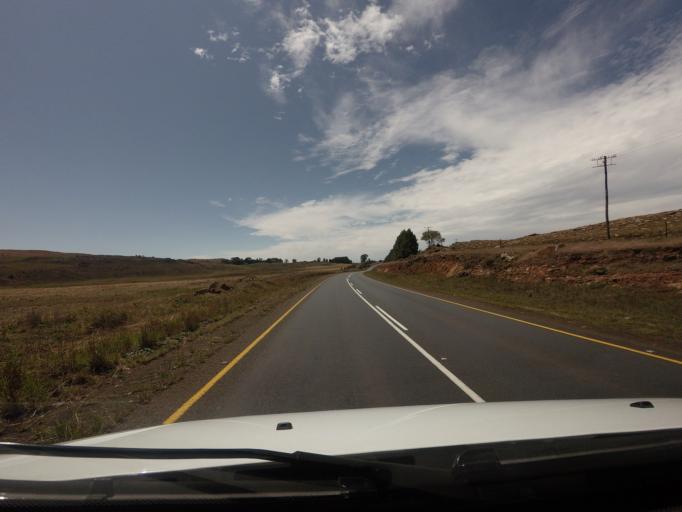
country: ZA
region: Mpumalanga
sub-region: Nkangala District Municipality
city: Belfast
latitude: -25.3822
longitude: 30.1342
